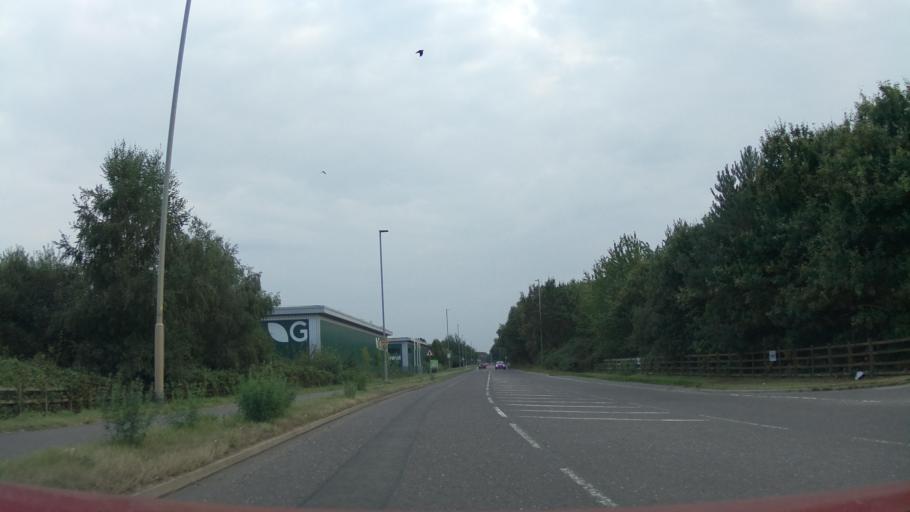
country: GB
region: England
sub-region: Lincolnshire
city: Skellingthorpe
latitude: 53.1533
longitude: -0.6709
